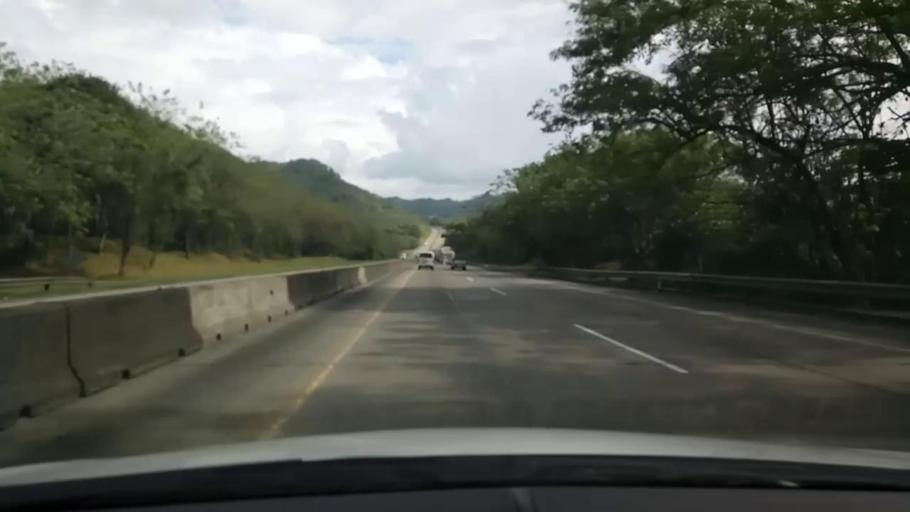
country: PA
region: Panama
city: Alcalde Diaz
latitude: 9.0827
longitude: -79.5963
